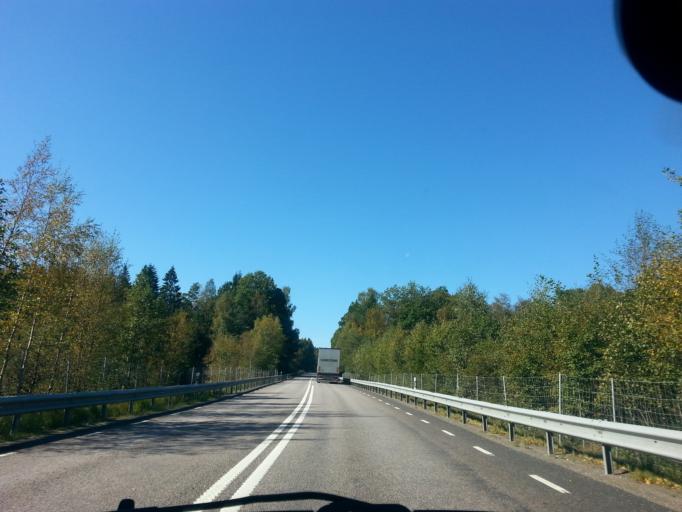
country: SE
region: Vaestra Goetaland
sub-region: Harryda Kommun
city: Hindas
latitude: 57.6533
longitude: 12.3923
